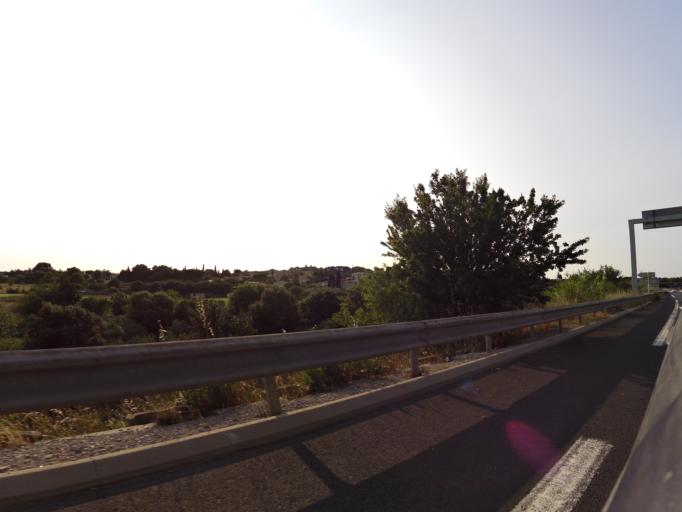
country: FR
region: Languedoc-Roussillon
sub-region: Departement du Gard
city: Gallargues-le-Montueux
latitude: 43.7199
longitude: 4.1821
